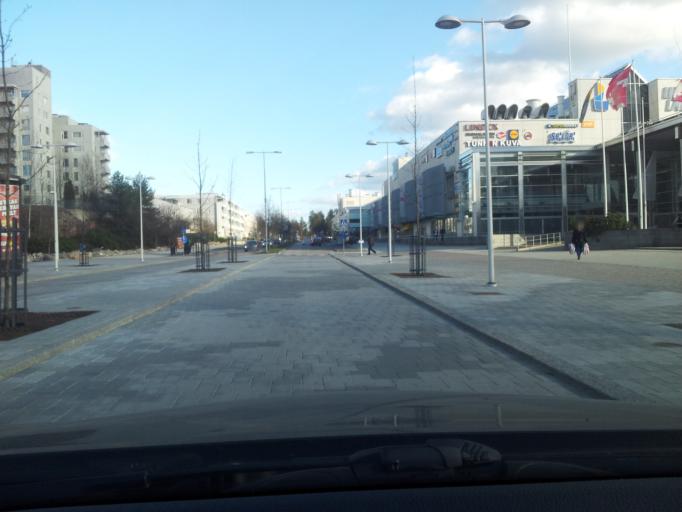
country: FI
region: Uusimaa
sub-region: Helsinki
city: Espoo
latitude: 60.1503
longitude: 24.6548
